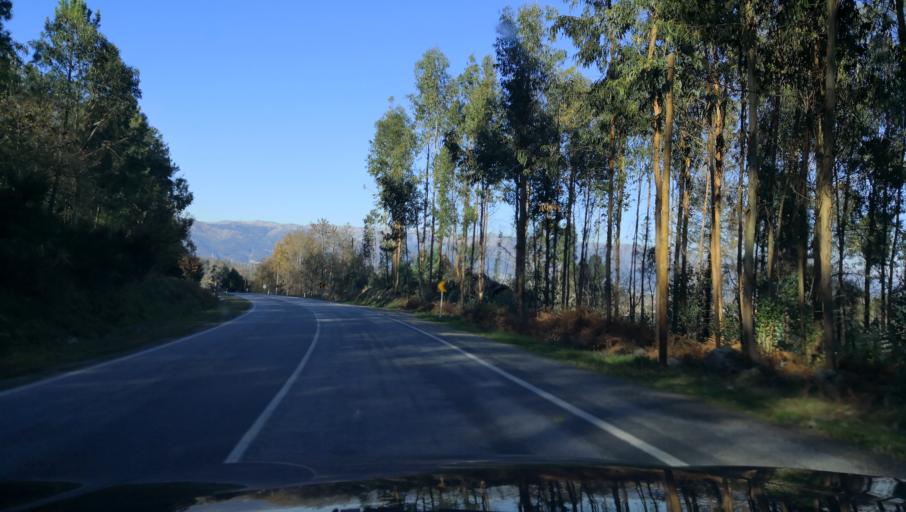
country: PT
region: Viseu
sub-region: Vouzela
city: Vouzela
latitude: 40.6981
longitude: -8.1387
